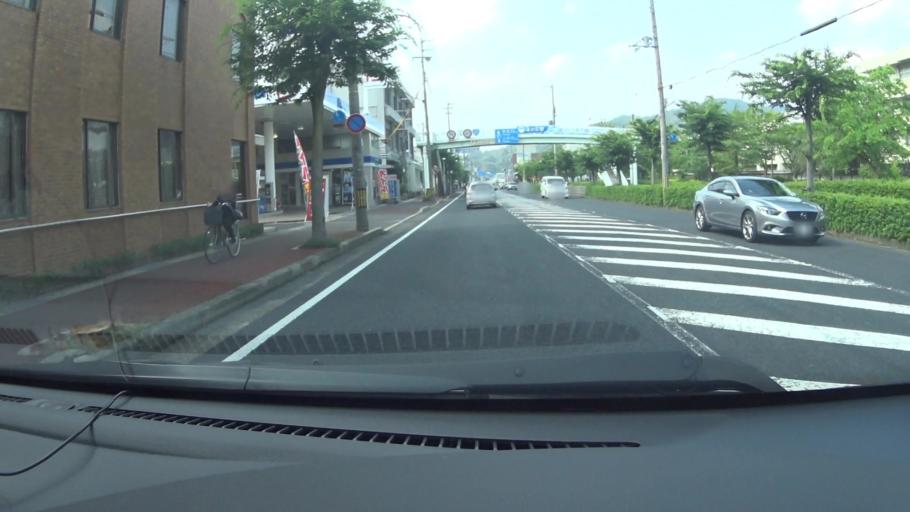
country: JP
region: Kyoto
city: Maizuru
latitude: 35.4465
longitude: 135.3286
